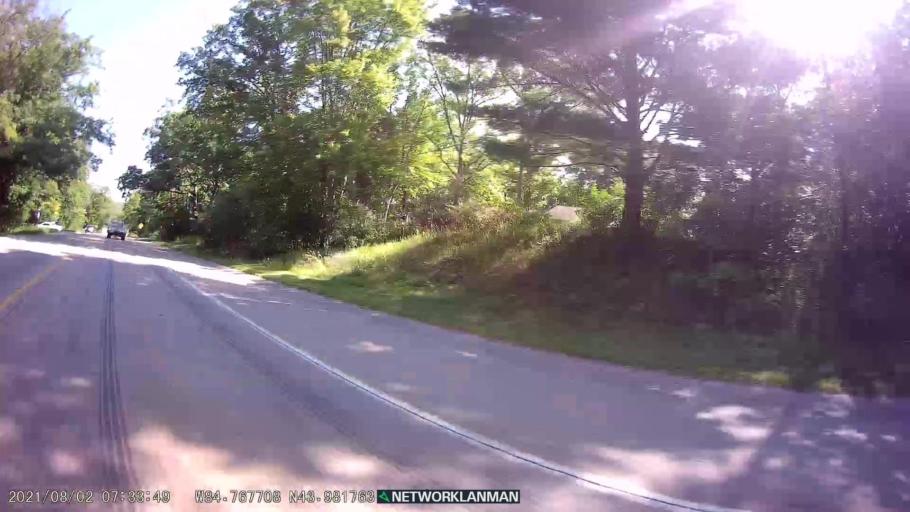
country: US
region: Michigan
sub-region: Clare County
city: Harrison
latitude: 43.9821
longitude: -84.7677
